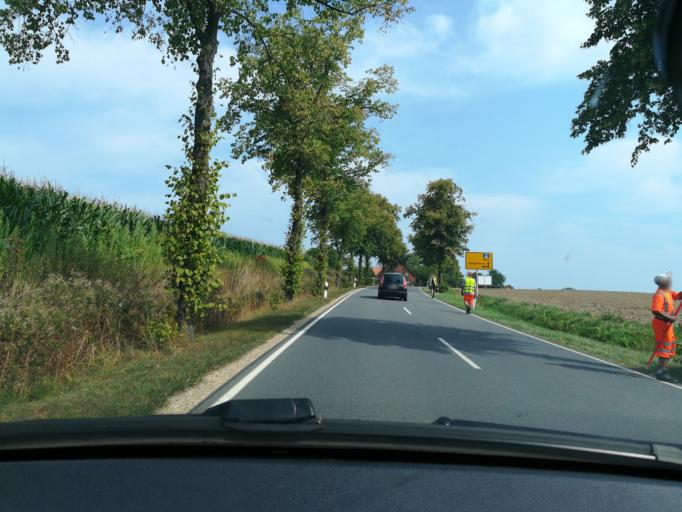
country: DE
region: North Rhine-Westphalia
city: Borgholzhausen
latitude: 52.1311
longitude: 8.3244
